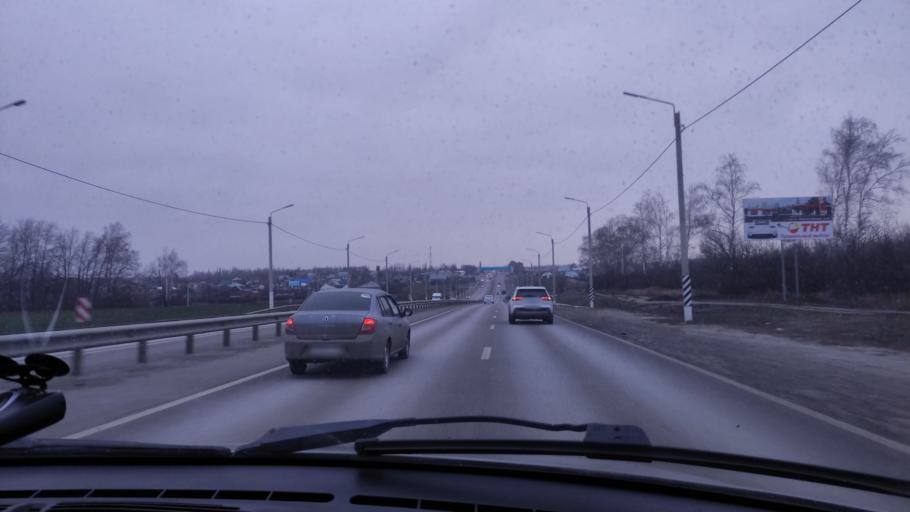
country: RU
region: Tambov
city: Komsomolets
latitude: 52.7277
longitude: 41.3334
